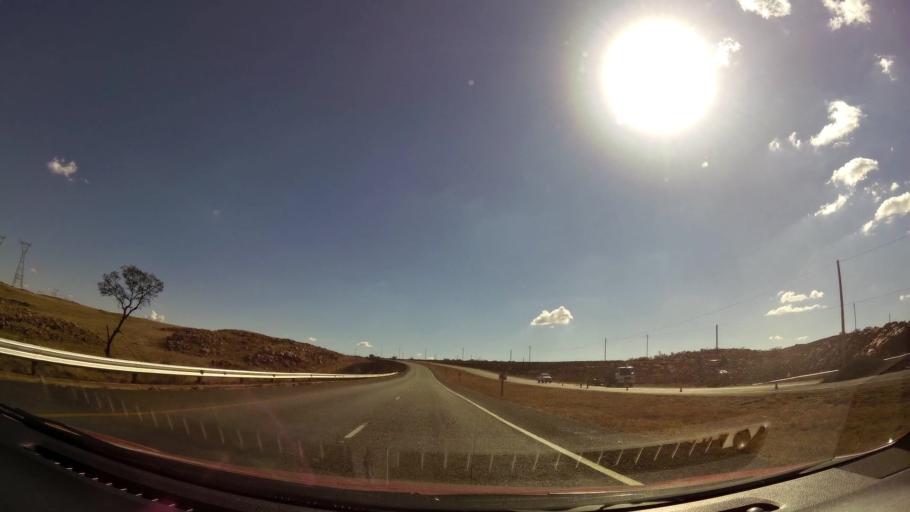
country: ZA
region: Gauteng
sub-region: West Rand District Municipality
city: Carletonville
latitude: -26.4169
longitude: 27.4556
